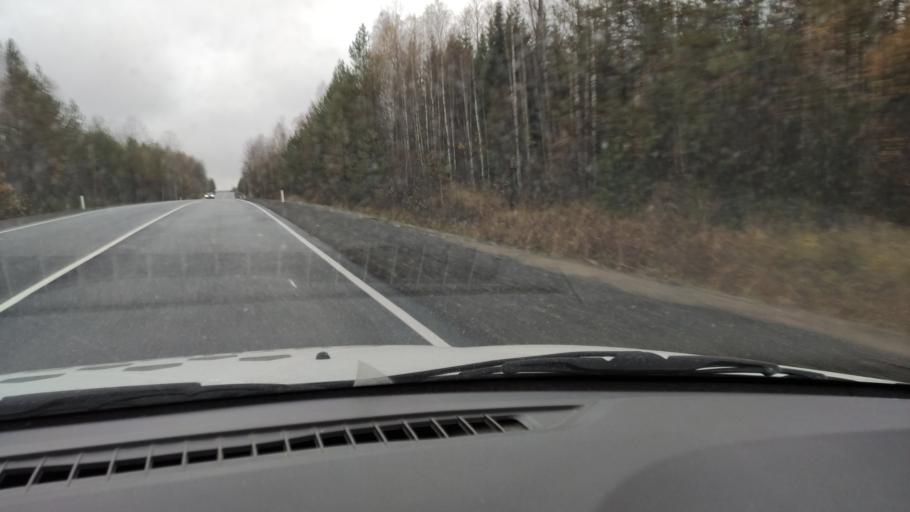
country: RU
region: Kirov
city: Chernaya Kholunitsa
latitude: 58.8728
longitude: 51.5176
